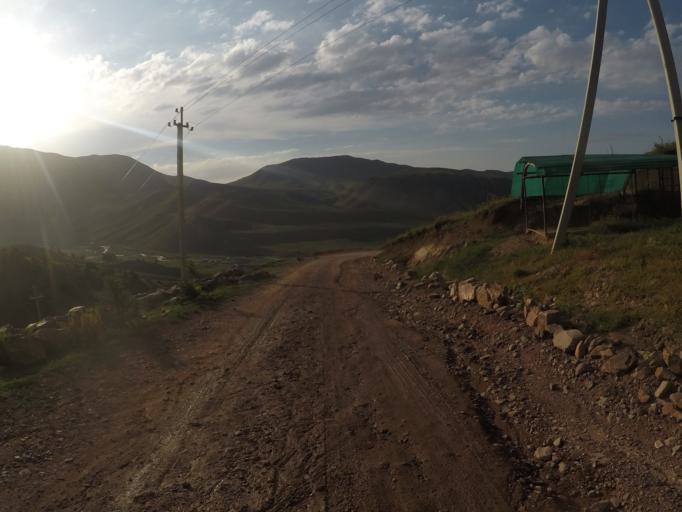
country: KG
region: Chuy
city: Bishkek
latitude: 42.6304
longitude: 74.6209
